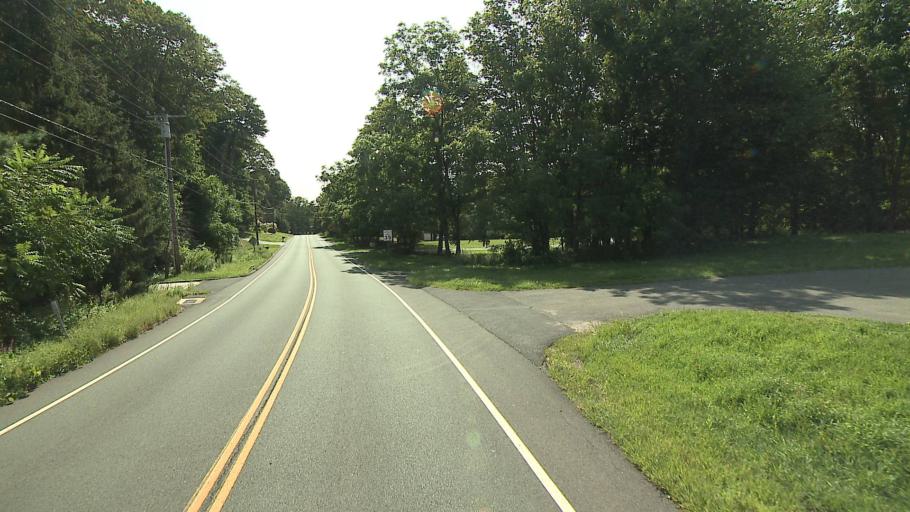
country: US
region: Connecticut
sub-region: Fairfield County
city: Newtown
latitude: 41.4397
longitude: -73.3689
